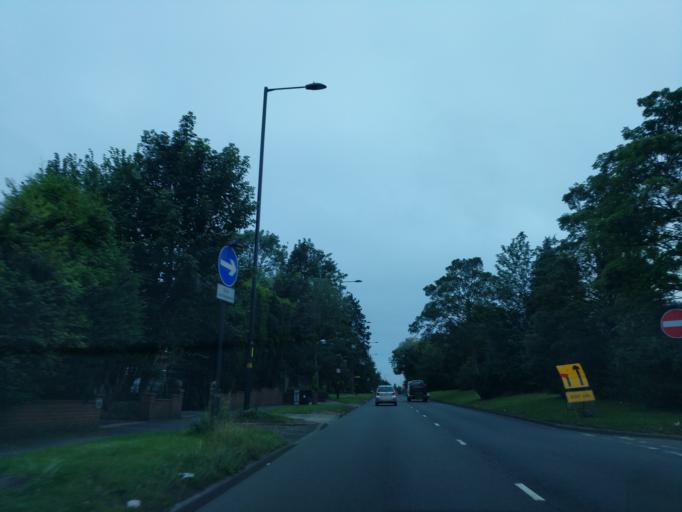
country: GB
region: England
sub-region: Sandwell
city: Smethwick
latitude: 52.4691
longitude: -1.9740
